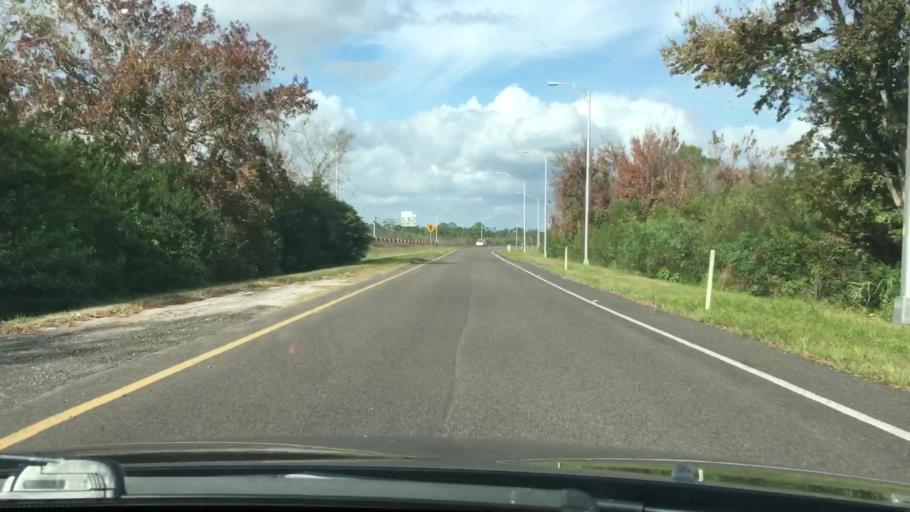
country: US
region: Florida
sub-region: Volusia County
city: Oak Hill
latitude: 28.7731
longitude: -80.8938
